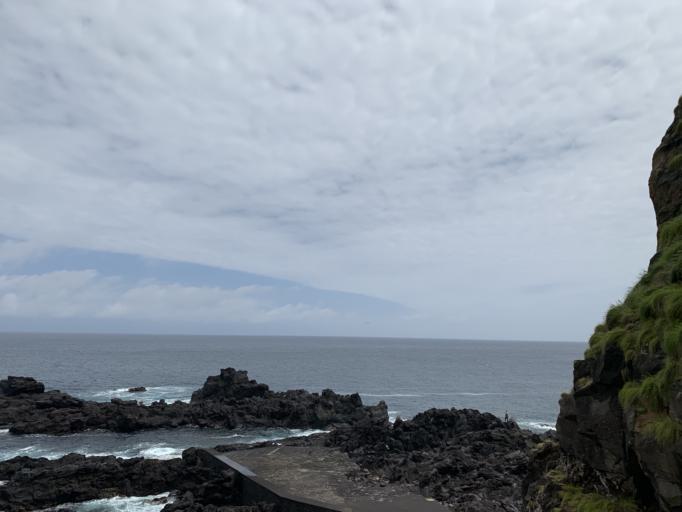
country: PT
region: Azores
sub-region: Ponta Delgada
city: Arrifes
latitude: 37.8994
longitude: -25.7501
